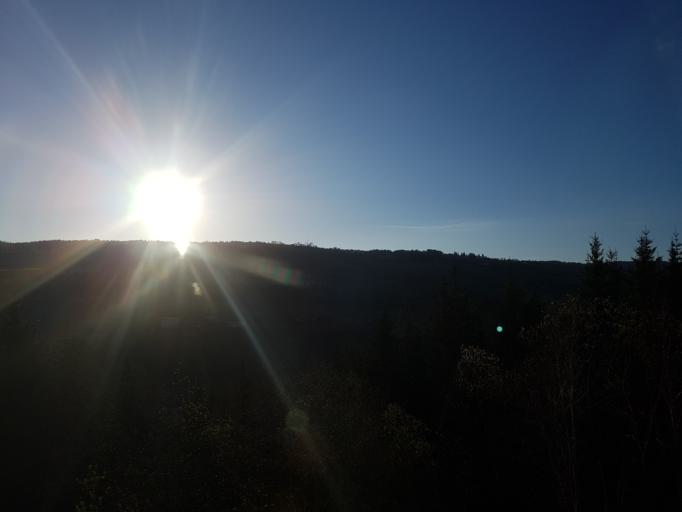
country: NO
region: Sor-Trondelag
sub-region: Midtre Gauldal
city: Storen
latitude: 62.9451
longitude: 10.1836
